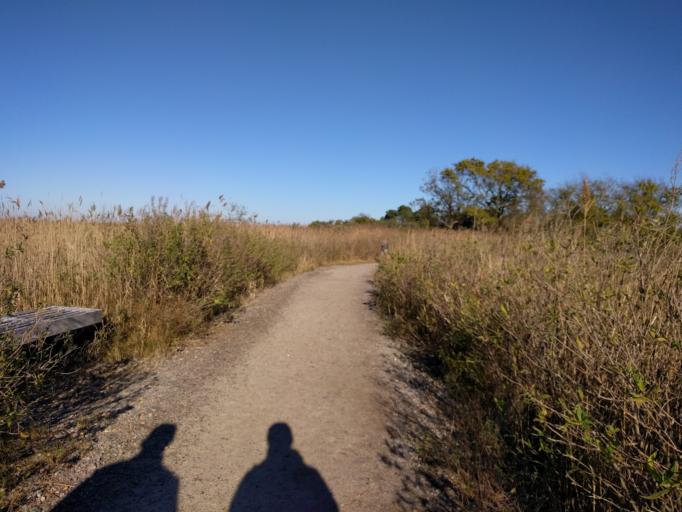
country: US
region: Virginia
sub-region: City of Hampton
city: East Hampton
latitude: 37.0825
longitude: -76.2763
